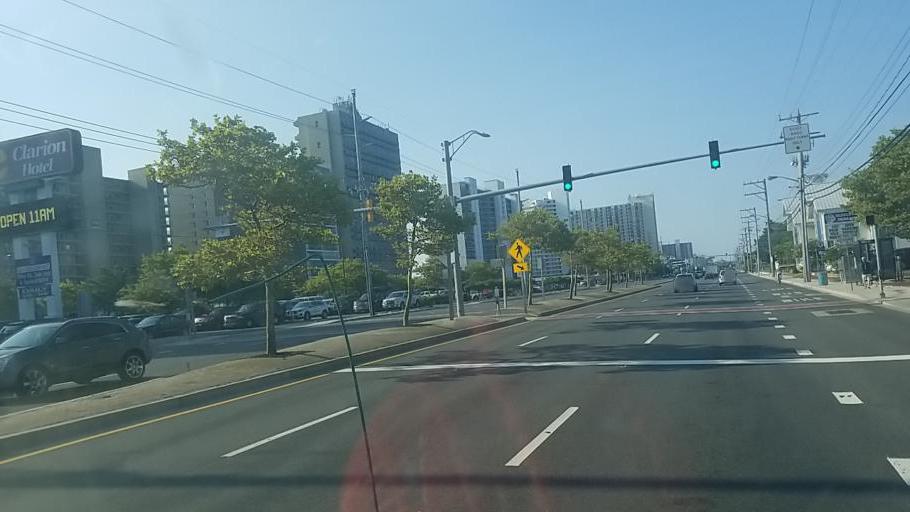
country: US
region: Maryland
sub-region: Worcester County
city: Ocean City
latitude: 38.4147
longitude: -75.0578
